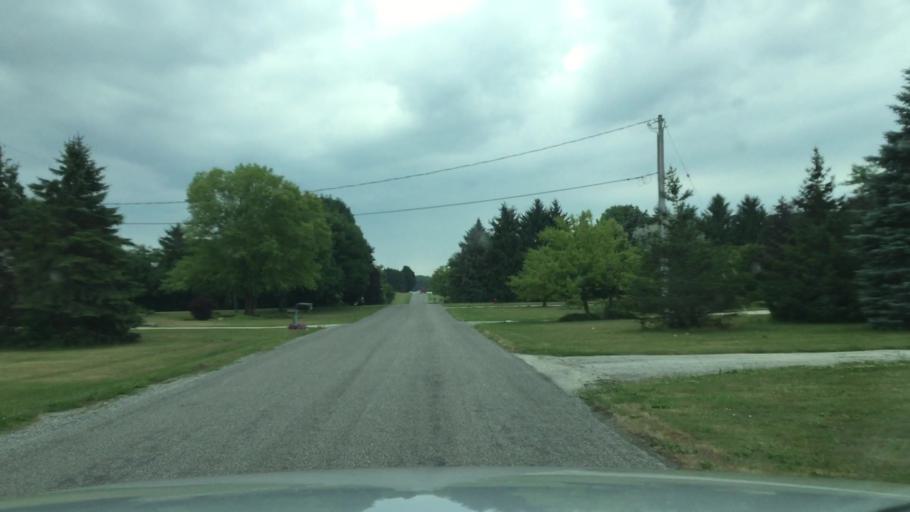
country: US
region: Michigan
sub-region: Saginaw County
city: Frankenmuth
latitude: 43.3132
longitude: -83.7956
